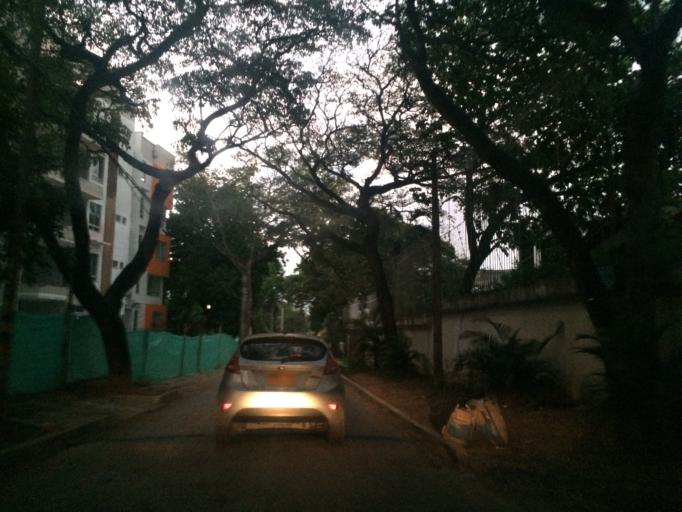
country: CO
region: Valle del Cauca
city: Jamundi
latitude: 3.3471
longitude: -76.5287
